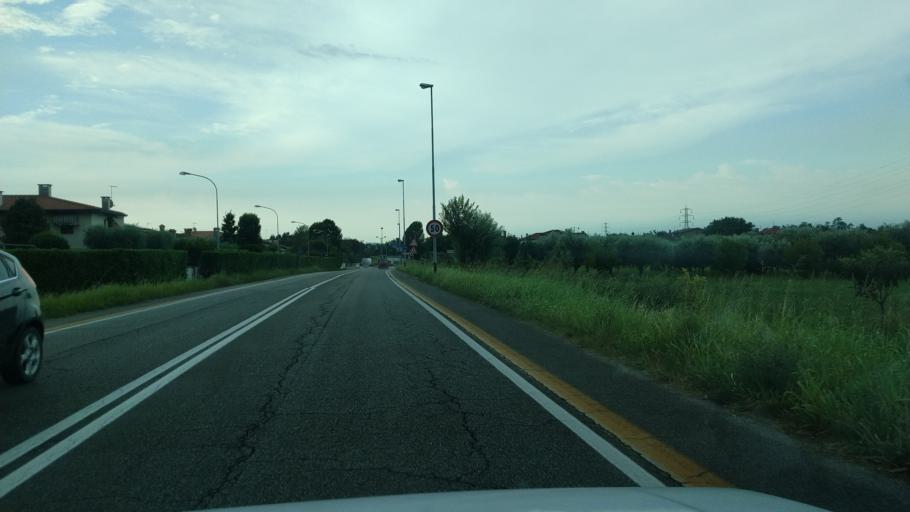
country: IT
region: Veneto
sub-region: Provincia di Vicenza
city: Bassano del Grappa
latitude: 45.7567
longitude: 11.7180
